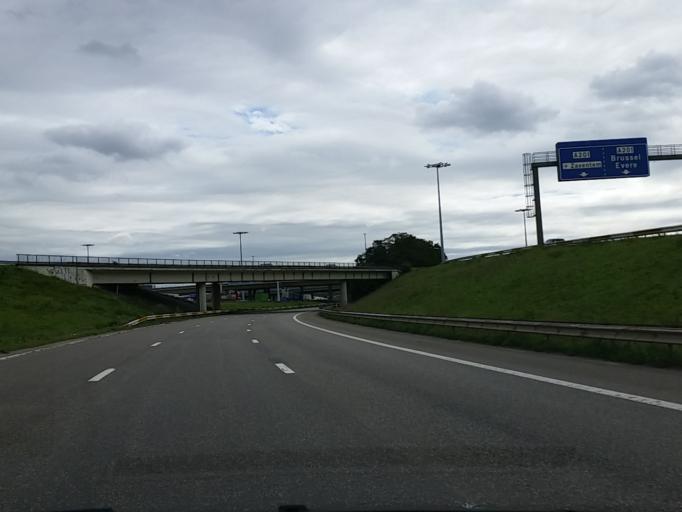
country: BE
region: Flanders
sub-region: Provincie Vlaams-Brabant
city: Diegem
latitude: 50.8941
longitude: 4.4489
